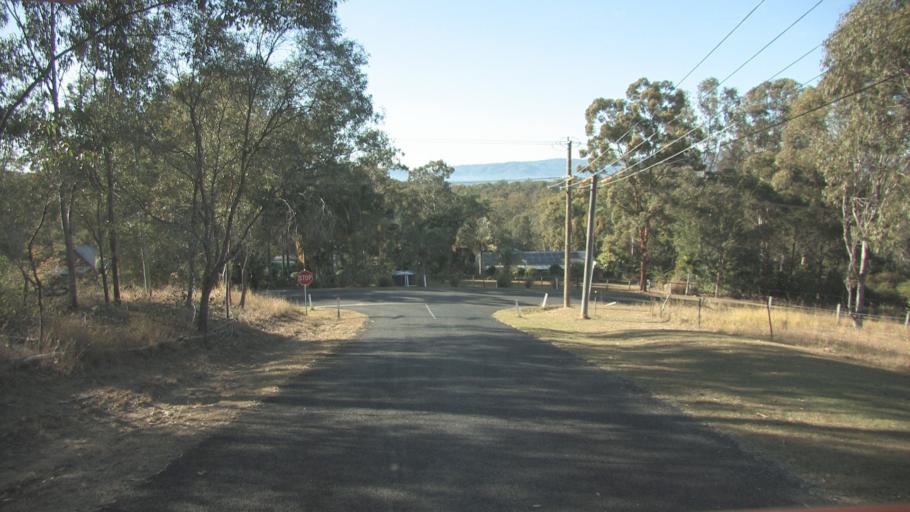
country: AU
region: Queensland
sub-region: Logan
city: Cedar Vale
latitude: -27.8409
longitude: 153.0828
